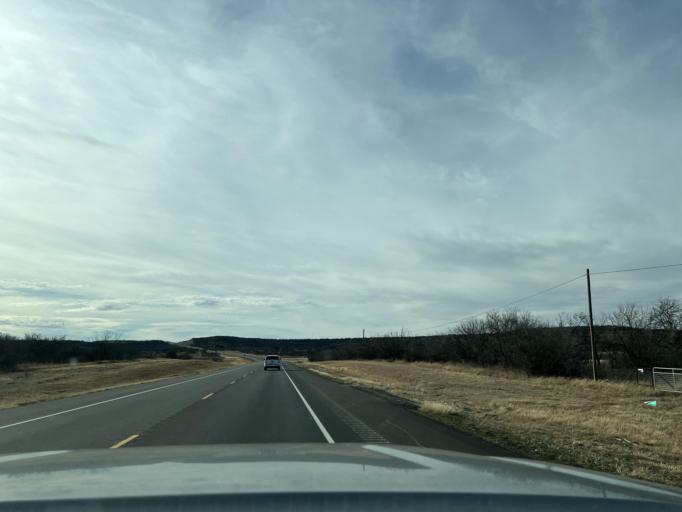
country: US
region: Texas
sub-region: Shackelford County
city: Albany
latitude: 32.7126
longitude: -99.3560
